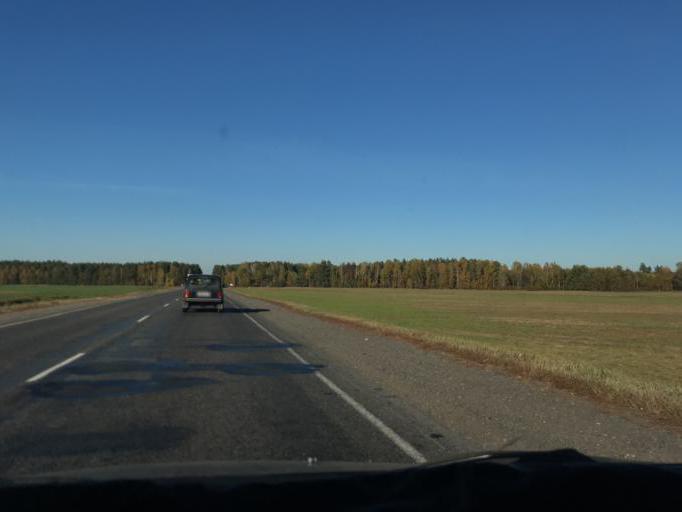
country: BY
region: Gomel
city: Kalinkavichy
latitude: 52.0497
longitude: 29.3611
